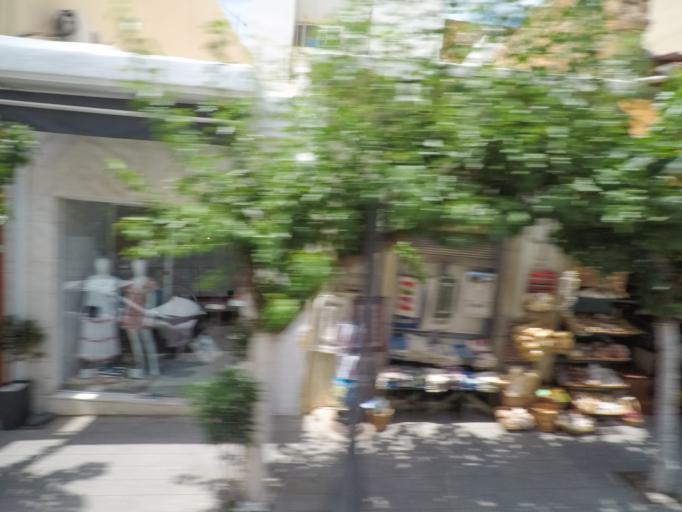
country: GR
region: Crete
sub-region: Nomos Lasithiou
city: Agios Nikolaos
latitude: 35.1887
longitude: 25.7170
